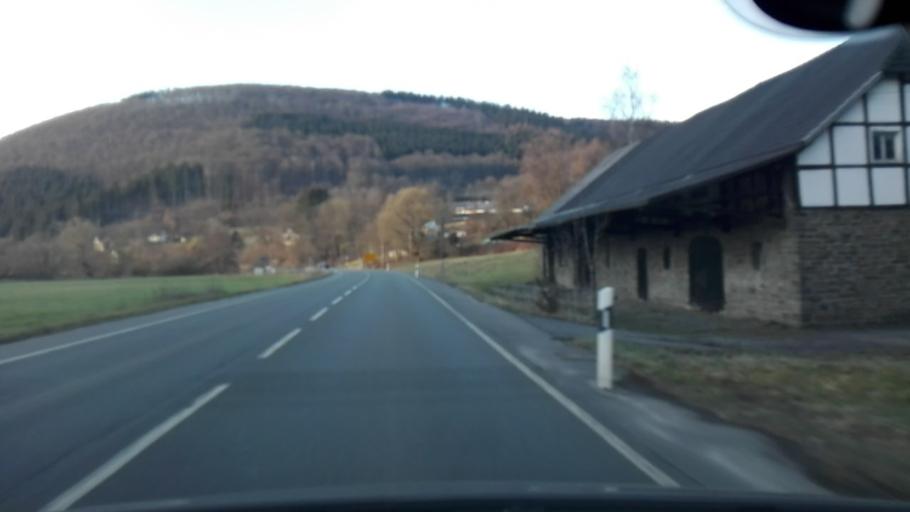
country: DE
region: North Rhine-Westphalia
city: Plettenberg
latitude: 51.2322
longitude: 7.8919
